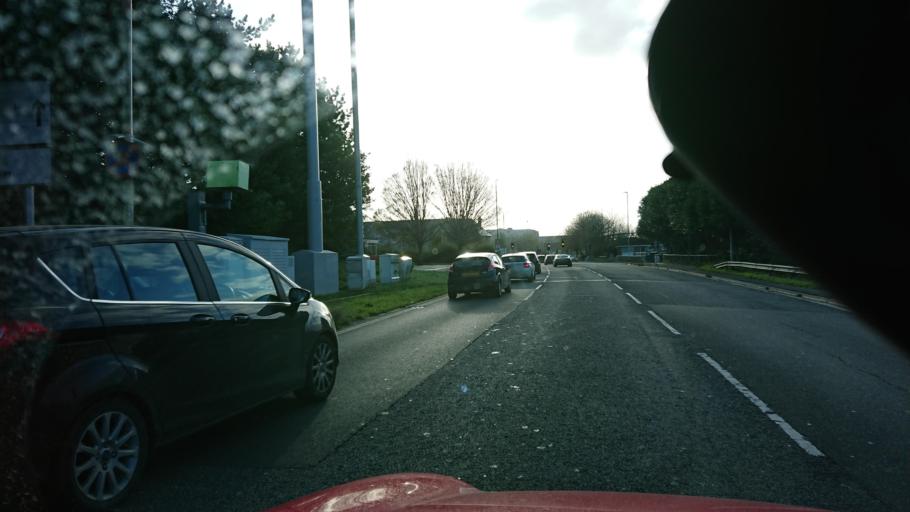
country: GB
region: England
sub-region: Cornwall
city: Torpoint
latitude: 50.3976
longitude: -4.1768
